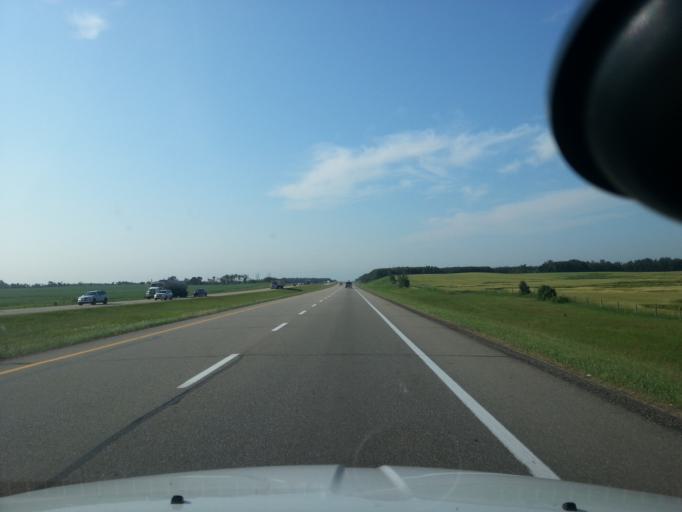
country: CA
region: Alberta
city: Ponoka
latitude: 52.7340
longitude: -113.6441
